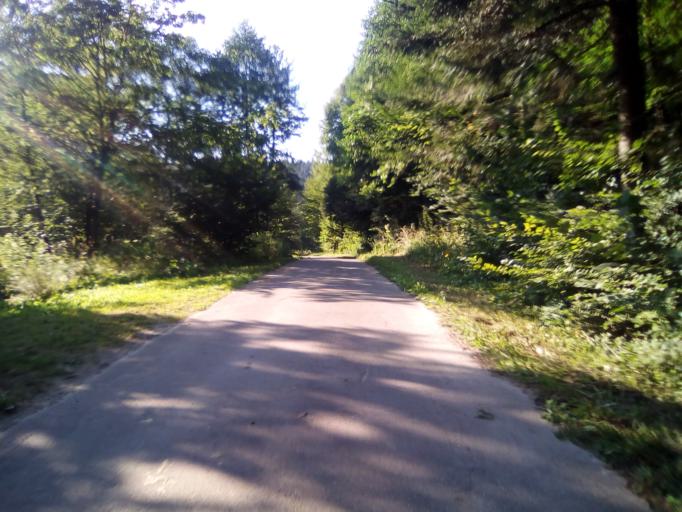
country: PL
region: Subcarpathian Voivodeship
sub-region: Powiat brzozowski
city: Domaradz
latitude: 49.8143
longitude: 21.9585
